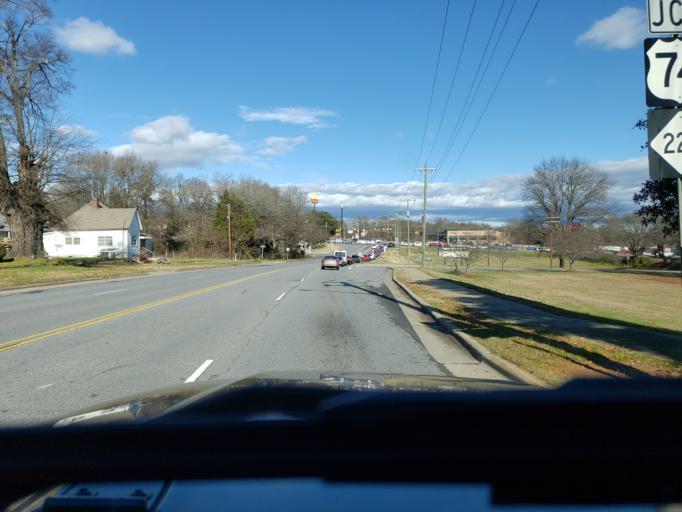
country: US
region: North Carolina
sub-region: Cleveland County
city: Shelby
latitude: 35.2757
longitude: -81.5399
